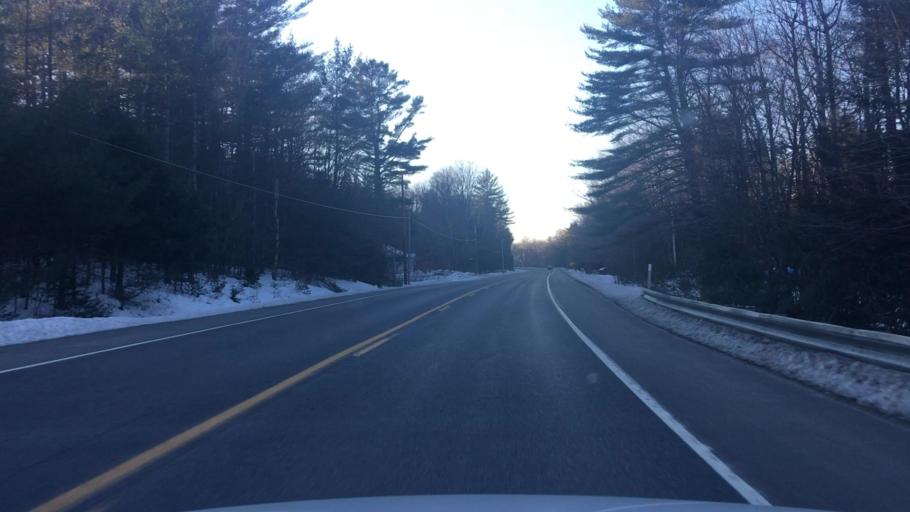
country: US
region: Maine
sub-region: Kennebec County
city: Rome
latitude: 44.6803
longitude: -69.8918
